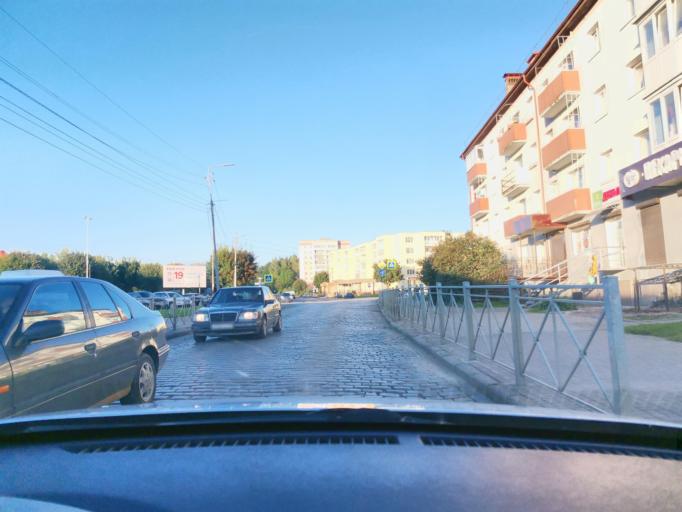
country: RU
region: Kaliningrad
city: Chernyakhovsk
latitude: 54.6369
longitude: 21.8078
